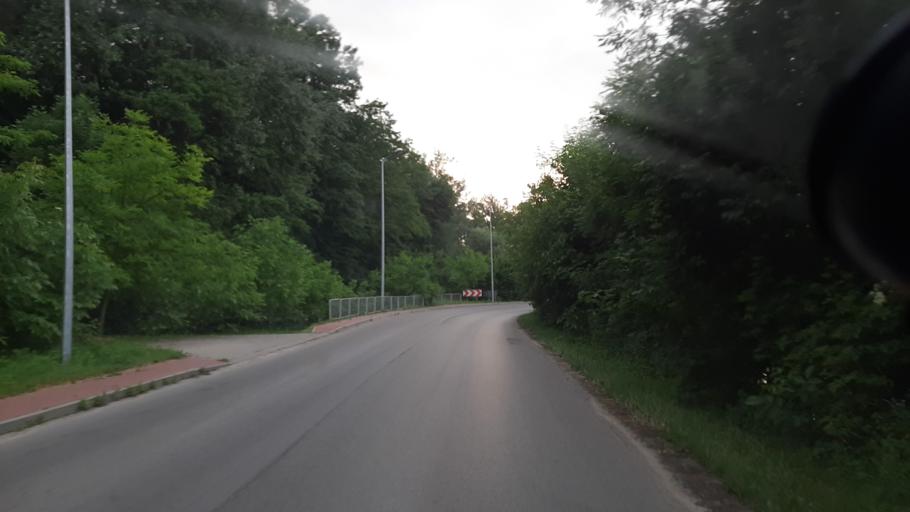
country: PL
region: Lublin Voivodeship
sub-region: Powiat lubelski
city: Garbow
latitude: 51.3518
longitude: 22.3322
